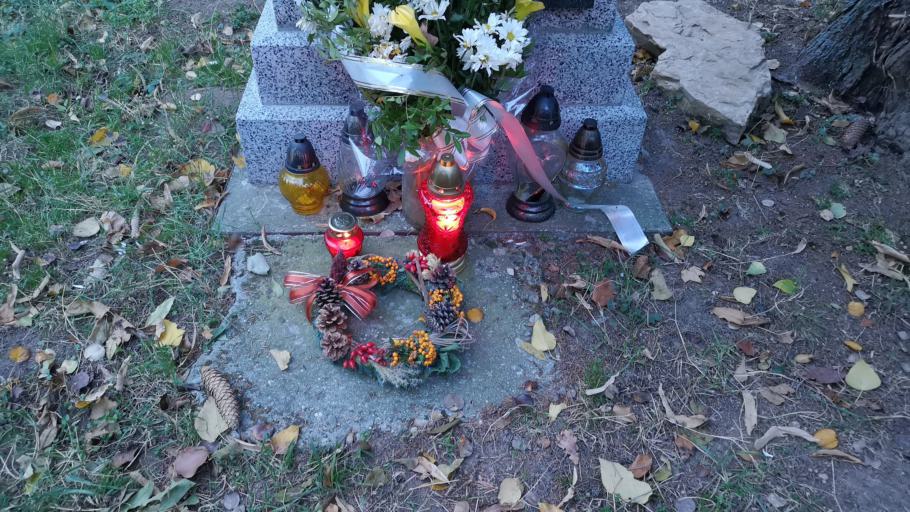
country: SK
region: Nitriansky
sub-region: Okres Nitra
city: Nitra
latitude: 48.2723
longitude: 18.0095
